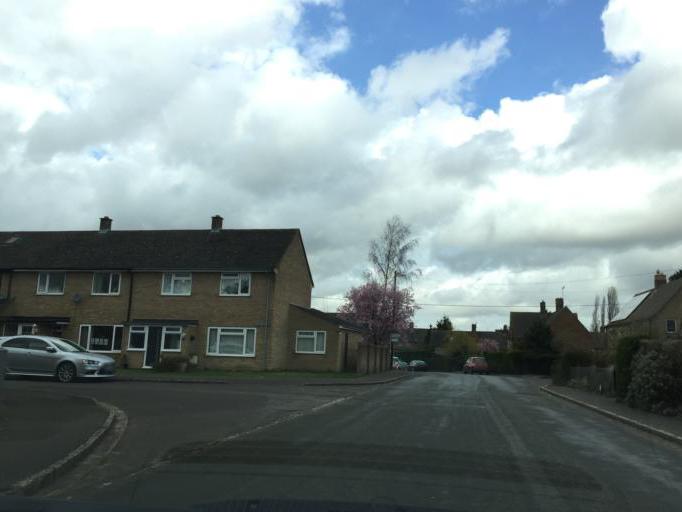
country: GB
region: England
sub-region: Oxfordshire
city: Stonesfield
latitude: 51.8547
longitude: -1.4280
